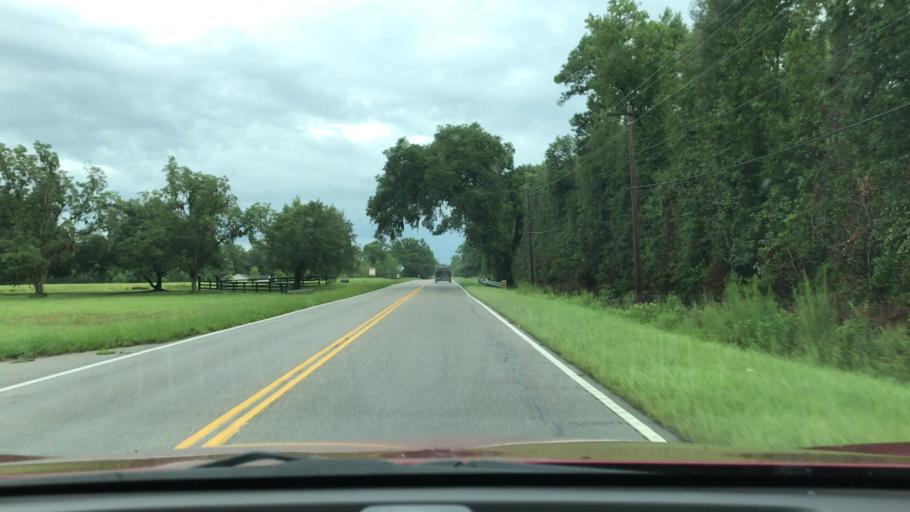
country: US
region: South Carolina
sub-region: Georgetown County
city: Georgetown
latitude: 33.4626
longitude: -79.2806
